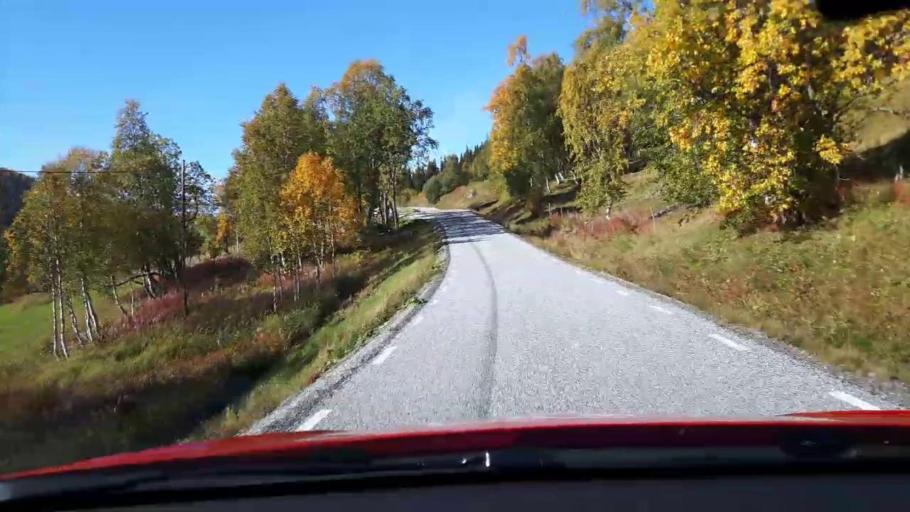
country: NO
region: Nord-Trondelag
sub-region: Royrvik
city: Royrvik
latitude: 64.8761
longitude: 14.2327
